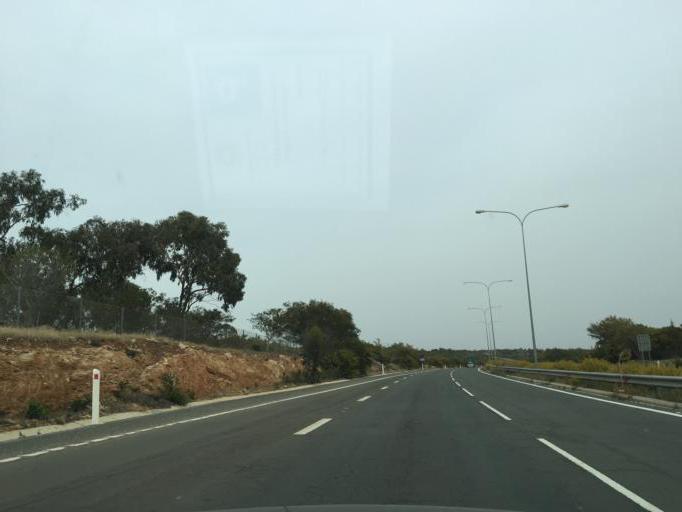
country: CY
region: Ammochostos
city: Ayia Napa
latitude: 34.9992
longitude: 33.9788
